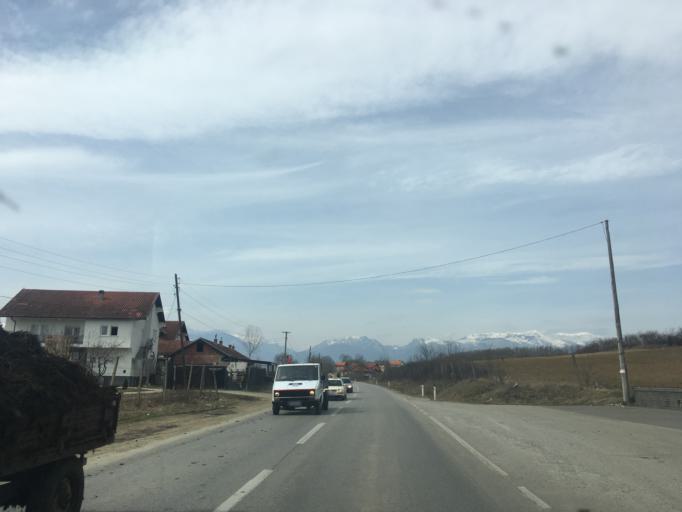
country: XK
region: Pec
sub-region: Komuna e Pejes
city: Kosuriq
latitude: 42.6222
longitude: 20.4741
